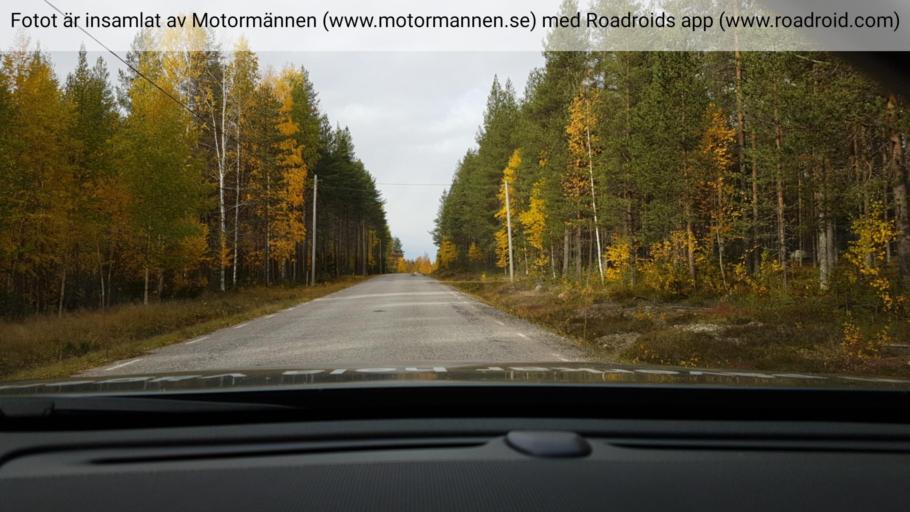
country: SE
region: Norrbotten
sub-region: Overkalix Kommun
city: OEverkalix
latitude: 66.2505
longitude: 23.1311
